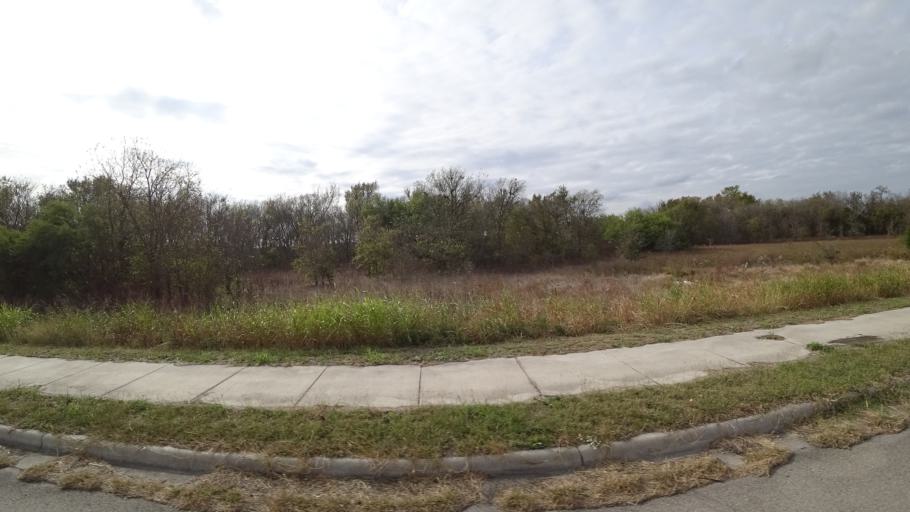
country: US
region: Texas
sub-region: Travis County
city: Wells Branch
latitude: 30.4278
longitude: -97.6572
